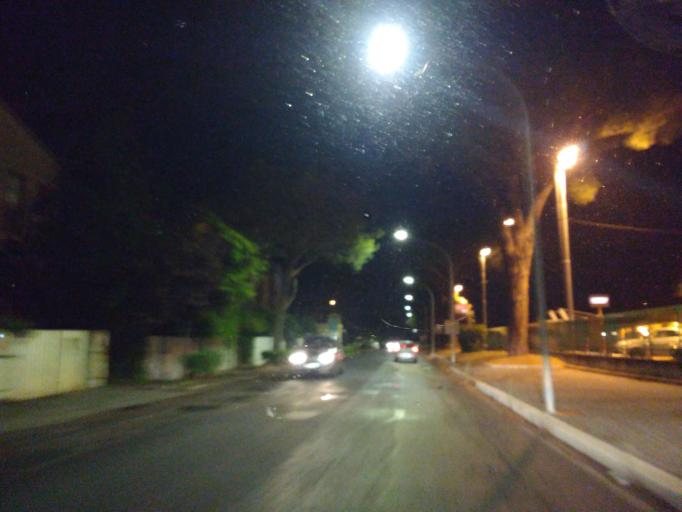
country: IT
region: Latium
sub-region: Citta metropolitana di Roma Capitale
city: Acilia-Castel Fusano-Ostia Antica
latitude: 41.7576
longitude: 12.3660
